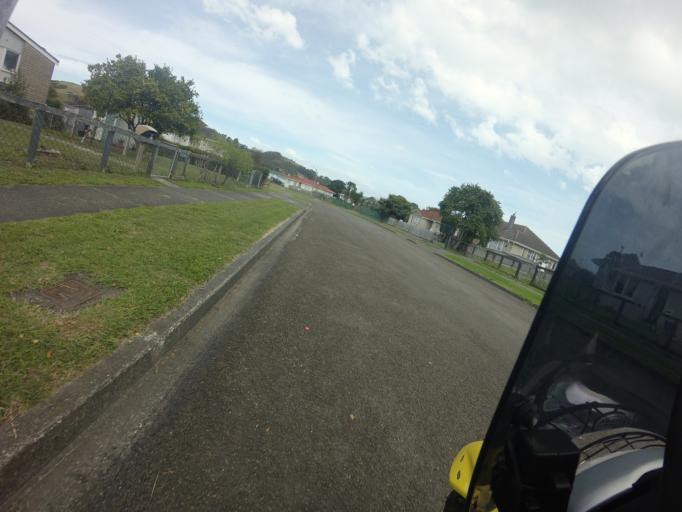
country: NZ
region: Gisborne
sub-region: Gisborne District
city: Gisborne
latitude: -38.6733
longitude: 178.0526
